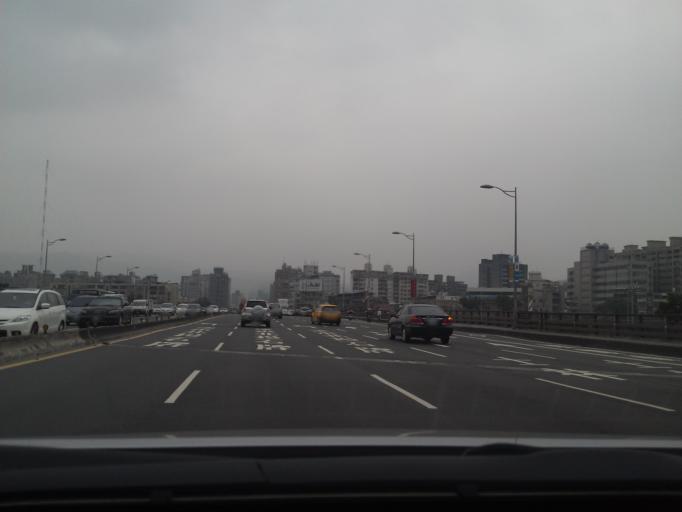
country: TW
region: Taipei
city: Taipei
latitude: 25.0883
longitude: 121.5126
